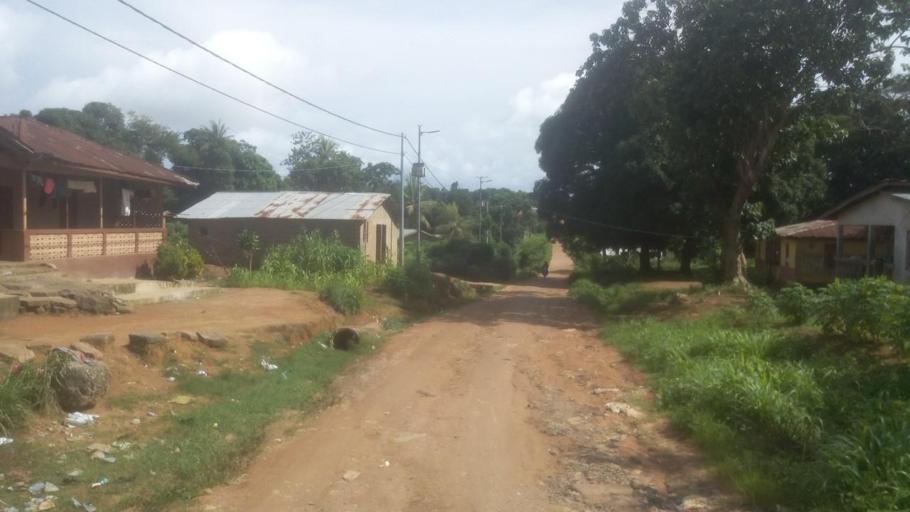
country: SL
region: Northern Province
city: Masoyila
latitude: 8.6120
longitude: -13.1942
